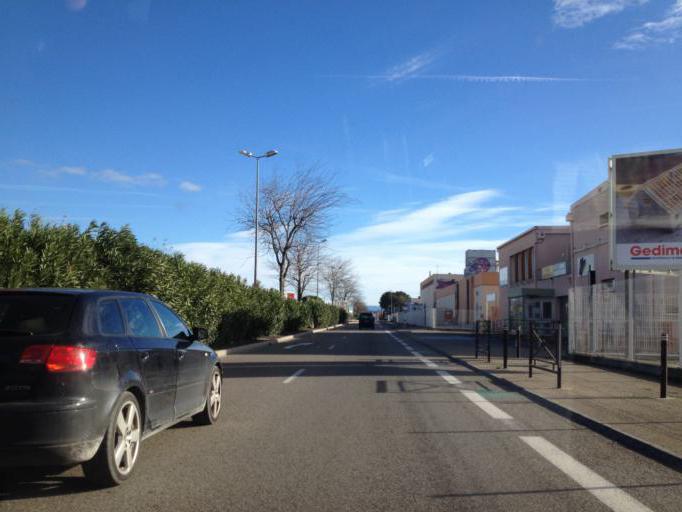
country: FR
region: Provence-Alpes-Cote d'Azur
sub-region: Departement du Vaucluse
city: Le Pontet
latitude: 43.9388
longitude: 4.8396
